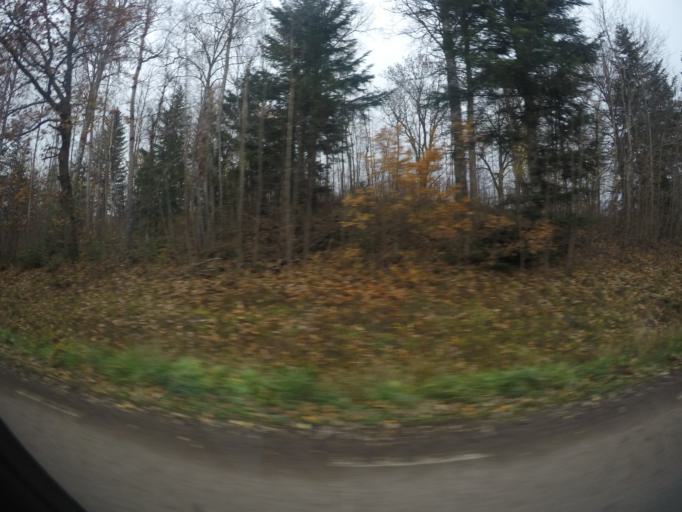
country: SE
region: Vaestmanland
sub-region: Surahammars Kommun
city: Ramnas
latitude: 59.6970
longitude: 16.0656
